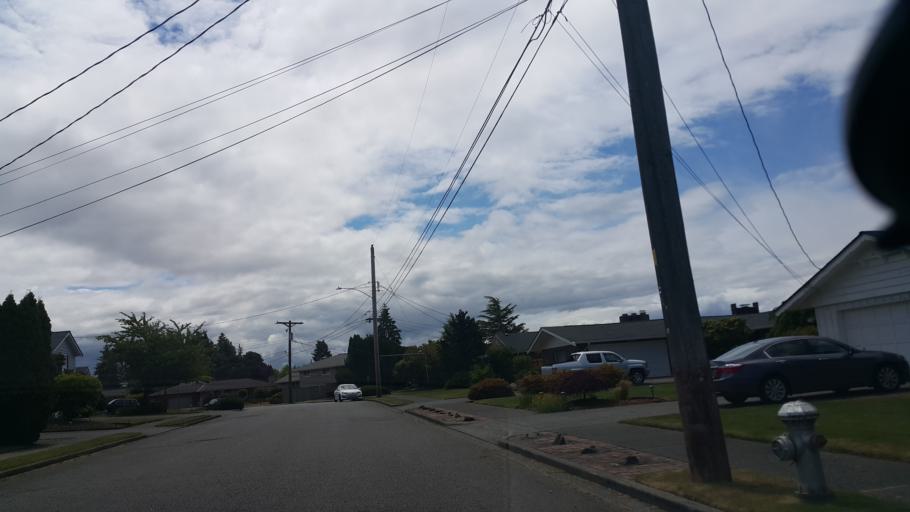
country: US
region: Washington
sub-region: Pierce County
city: University Place
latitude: 47.2485
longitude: -122.5357
